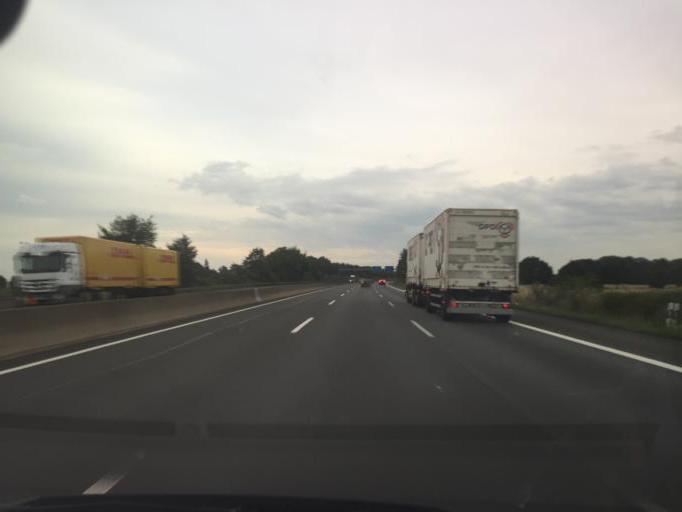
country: DE
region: North Rhine-Westphalia
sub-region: Regierungsbezirk Koln
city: Titz
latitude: 51.0585
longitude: 6.4434
